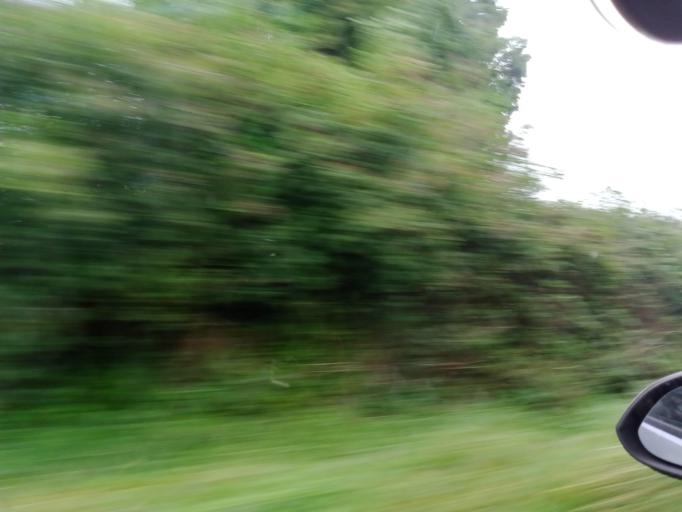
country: IE
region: Leinster
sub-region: Kilkenny
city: Castlecomer
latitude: 52.8490
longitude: -7.1771
